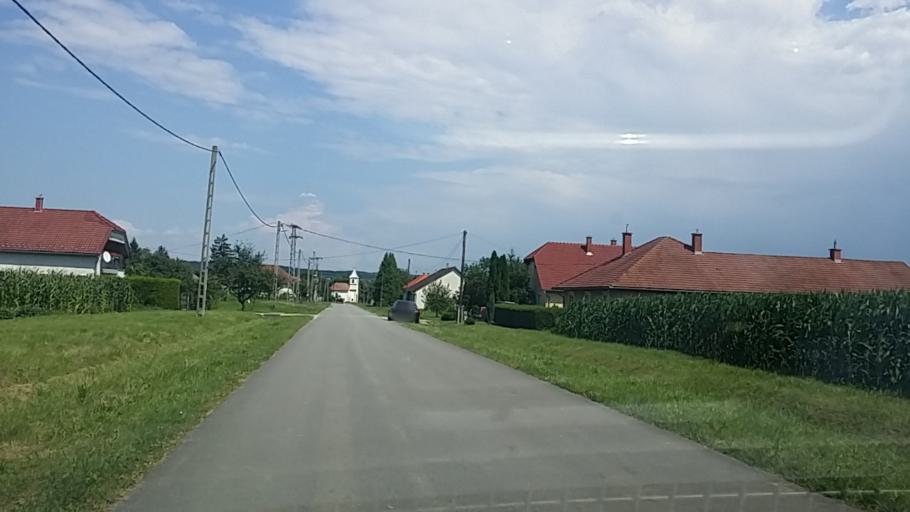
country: HU
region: Zala
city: Lenti
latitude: 46.5466
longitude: 16.5586
